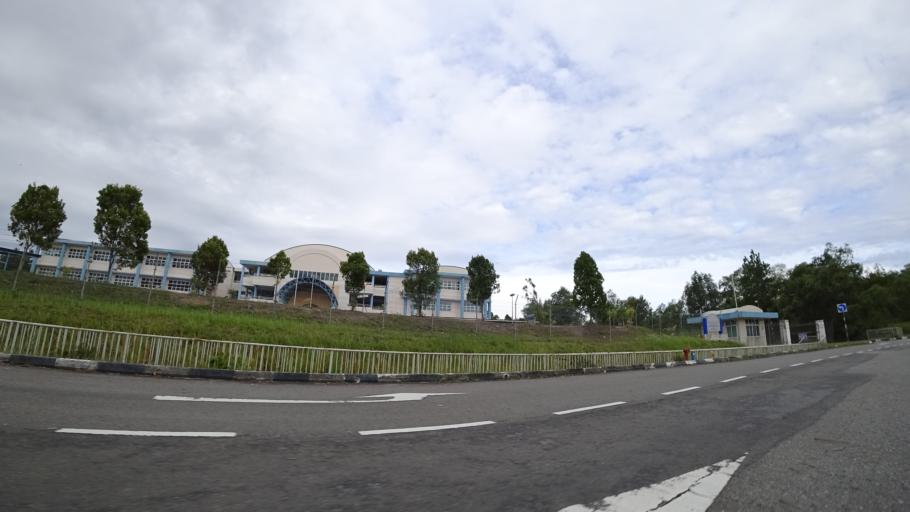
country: BN
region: Brunei and Muara
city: Bandar Seri Begawan
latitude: 4.9302
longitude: 114.9520
